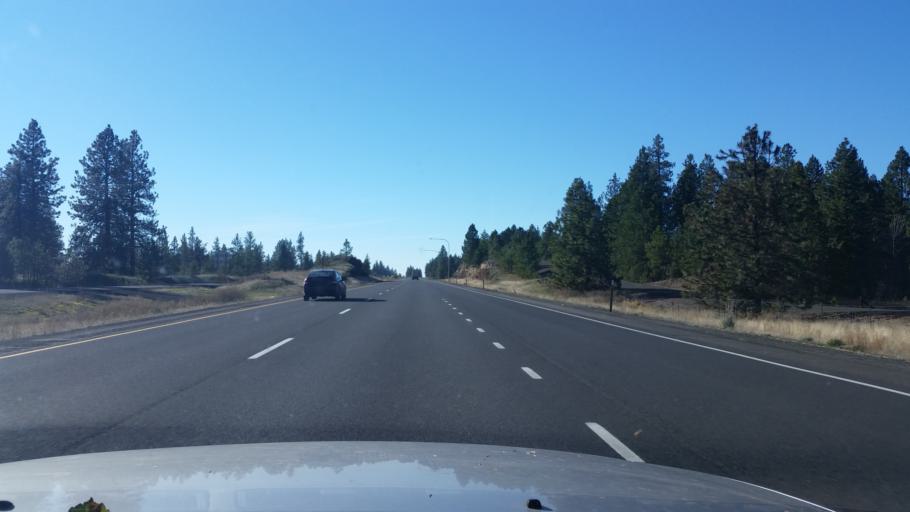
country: US
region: Washington
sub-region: Spokane County
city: Medical Lake
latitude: 47.4347
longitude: -117.7930
